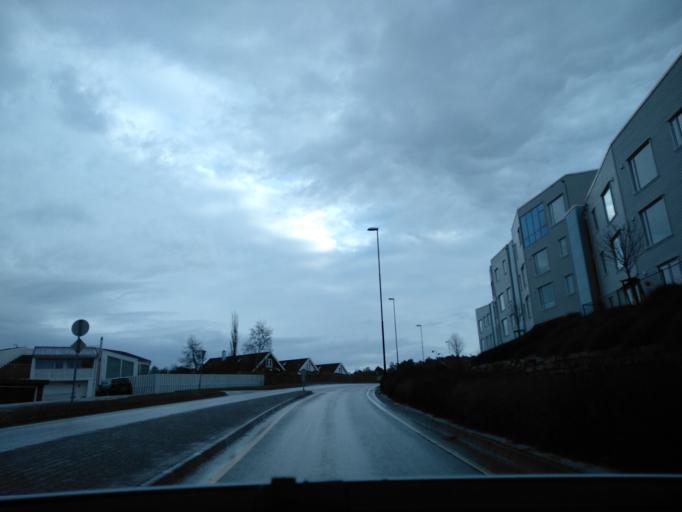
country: NO
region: Rogaland
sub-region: Stavanger
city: Stavanger
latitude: 58.9891
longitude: 5.6906
